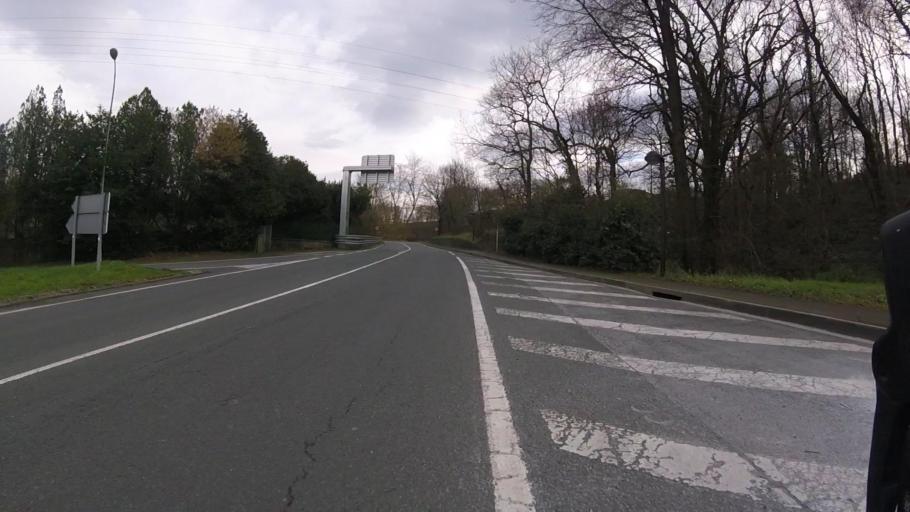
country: ES
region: Basque Country
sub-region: Provincia de Guipuzcoa
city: Lezo
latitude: 43.3060
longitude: -1.8787
